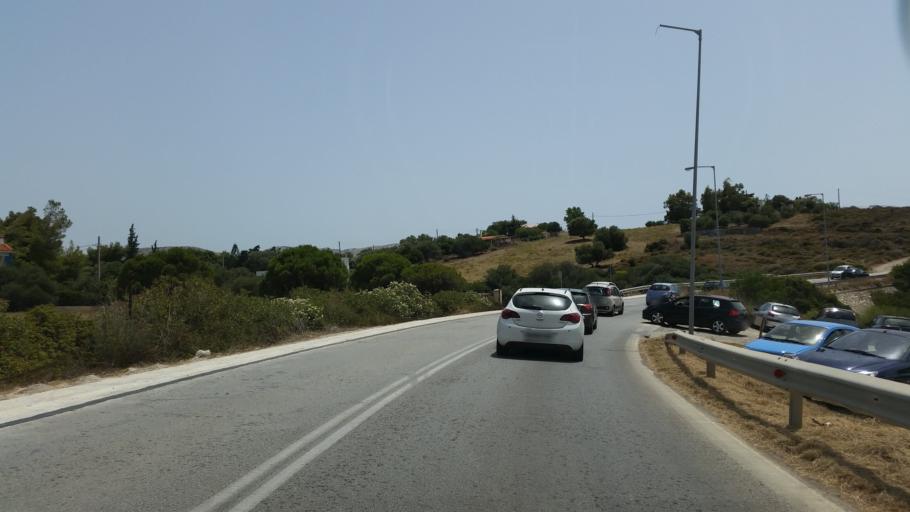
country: GR
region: Attica
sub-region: Nomarchia Anatolikis Attikis
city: Palaia Fokaia
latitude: 37.7011
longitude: 23.9402
